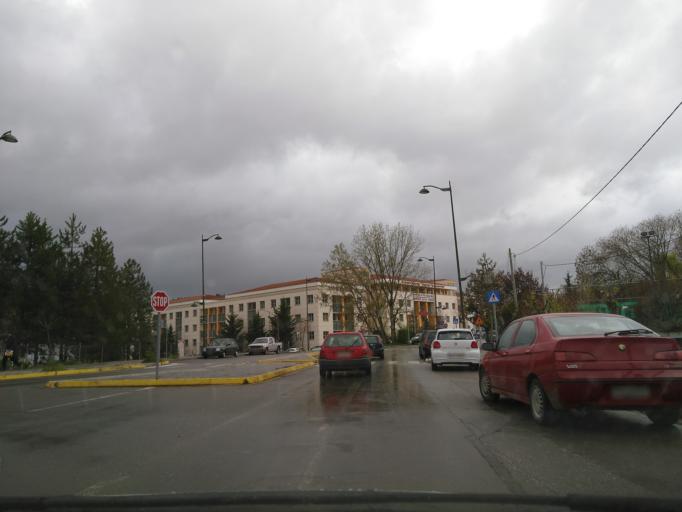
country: GR
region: West Macedonia
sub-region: Nomos Grevenon
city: Grevena
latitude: 40.0861
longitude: 21.4388
